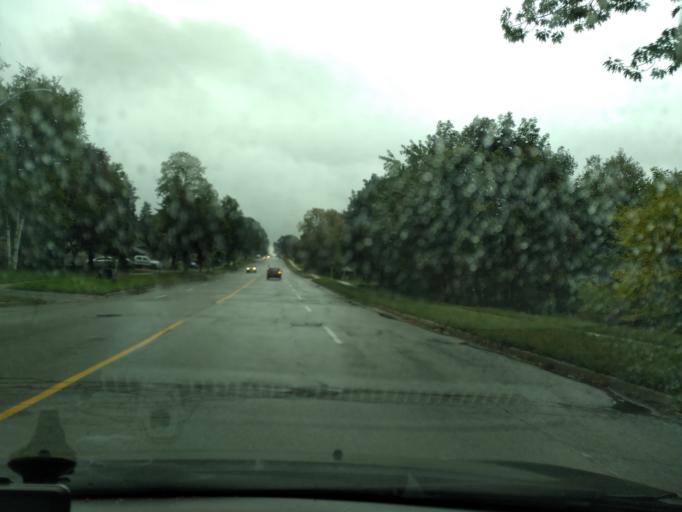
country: CA
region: Ontario
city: Barrie
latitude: 44.4058
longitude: -79.6746
